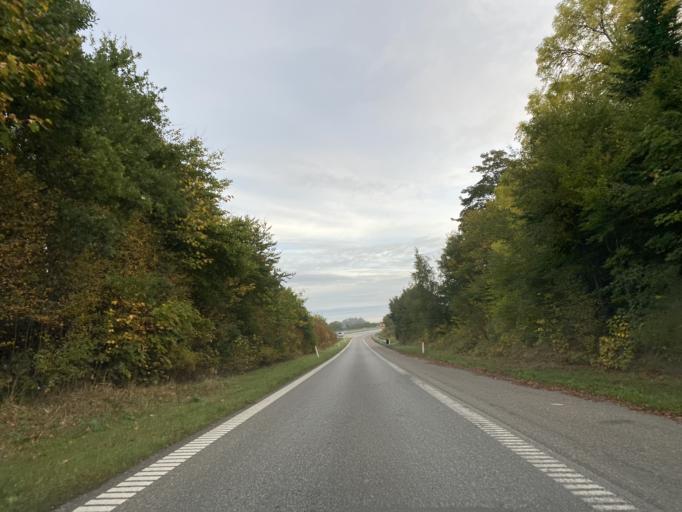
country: DK
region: Central Jutland
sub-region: Arhus Kommune
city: Kolt
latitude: 56.1087
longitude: 10.0540
